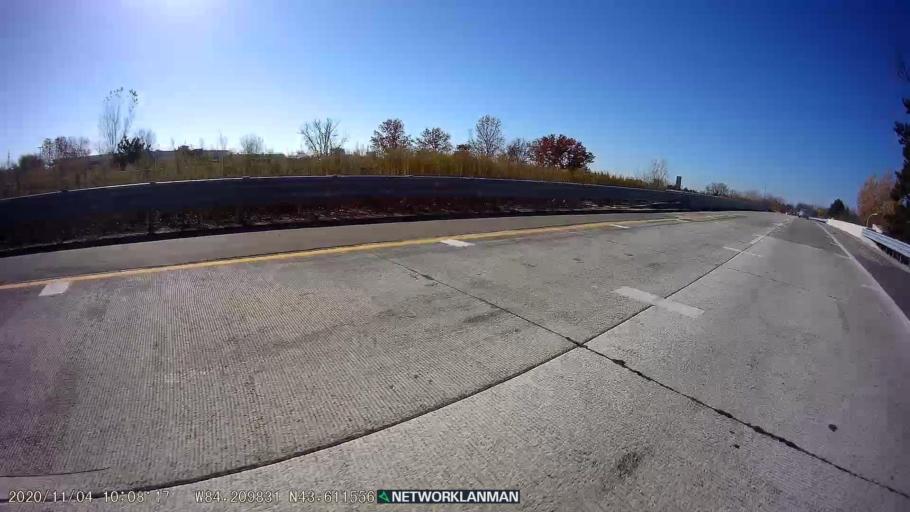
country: US
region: Michigan
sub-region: Midland County
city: Midland
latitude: 43.6116
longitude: -84.2101
